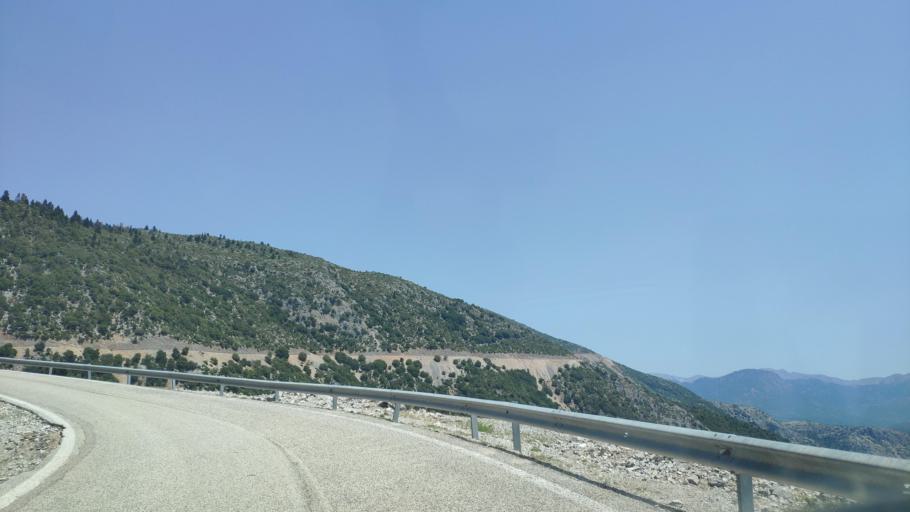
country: GR
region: West Greece
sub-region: Nomos Aitolias kai Akarnanias
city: Krikellos
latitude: 39.0283
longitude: 21.3702
